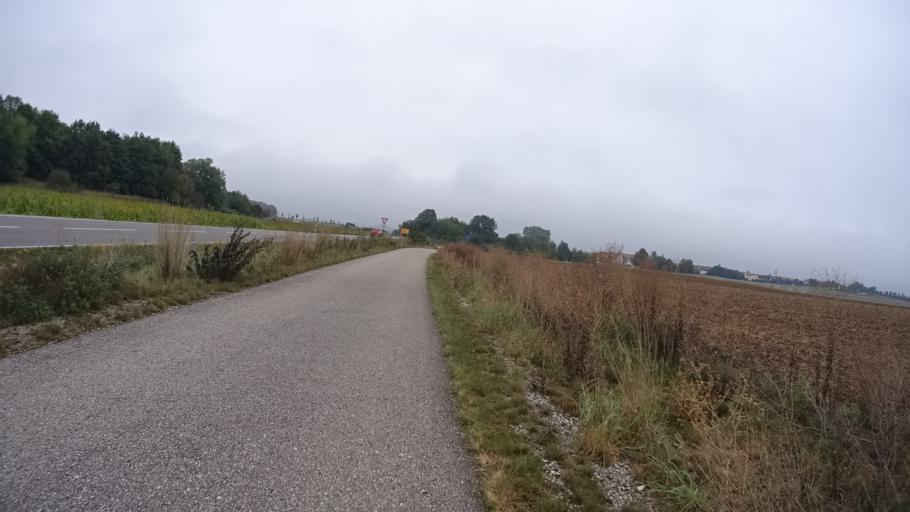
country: DE
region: Bavaria
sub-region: Upper Bavaria
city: Wettstetten
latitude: 48.8147
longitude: 11.4071
